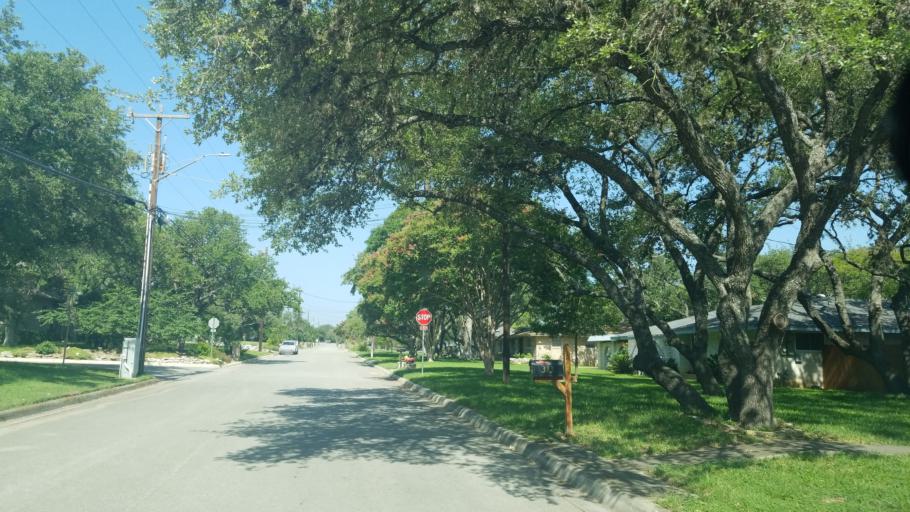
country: US
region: Texas
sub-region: Bexar County
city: Hollywood Park
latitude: 29.6047
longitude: -98.4842
